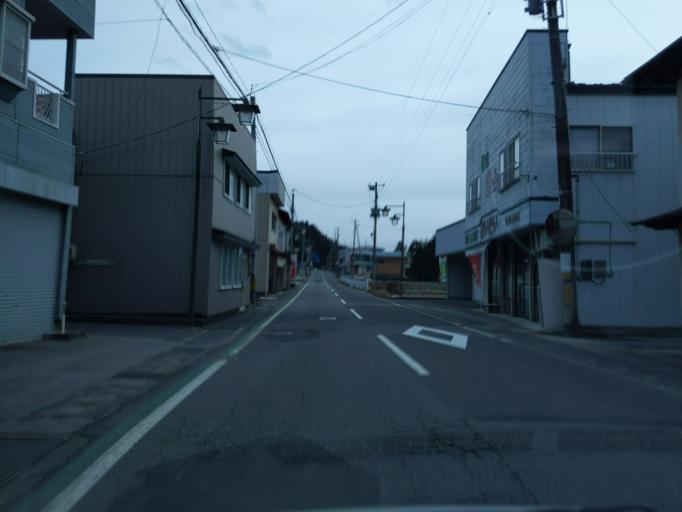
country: JP
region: Iwate
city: Mizusawa
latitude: 39.0361
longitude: 141.2947
